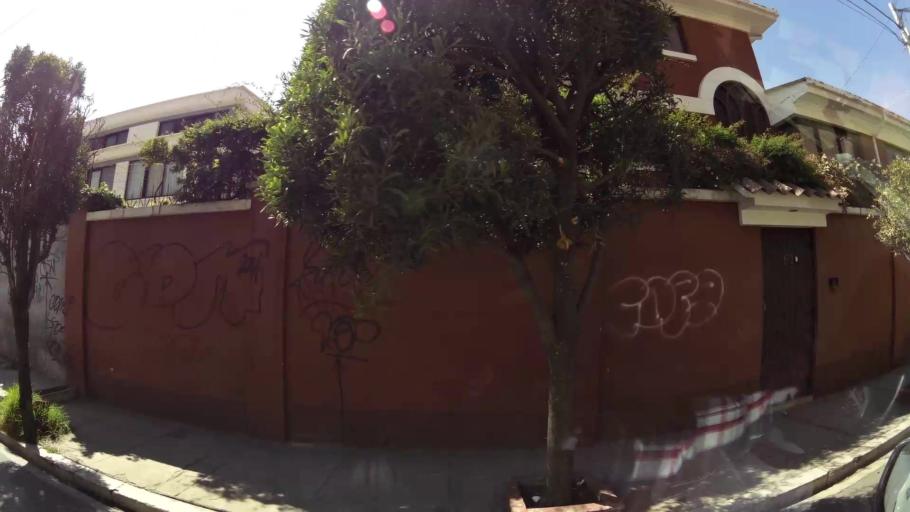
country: BO
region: La Paz
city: La Paz
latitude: -16.5303
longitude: -68.0877
